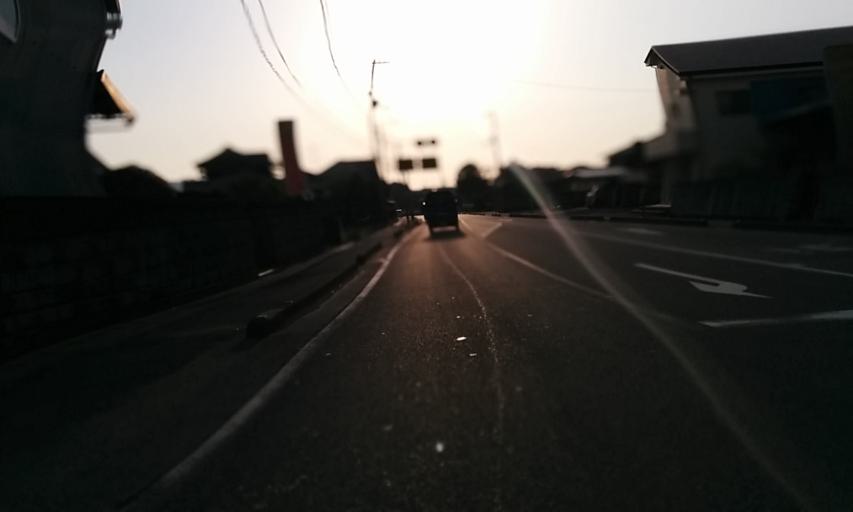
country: JP
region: Ehime
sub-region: Shikoku-chuo Shi
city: Matsuyama
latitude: 33.7814
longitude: 132.8142
